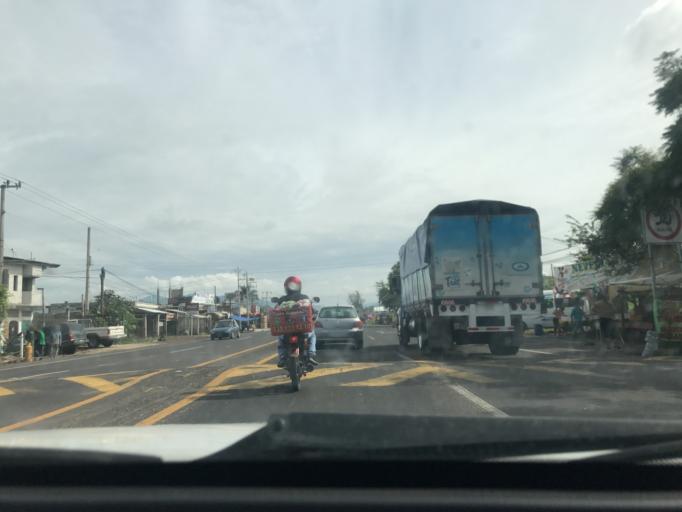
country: MX
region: Morelos
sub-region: Atlatlahucan
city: Colonia San Francisco
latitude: 18.8842
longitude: -98.9175
